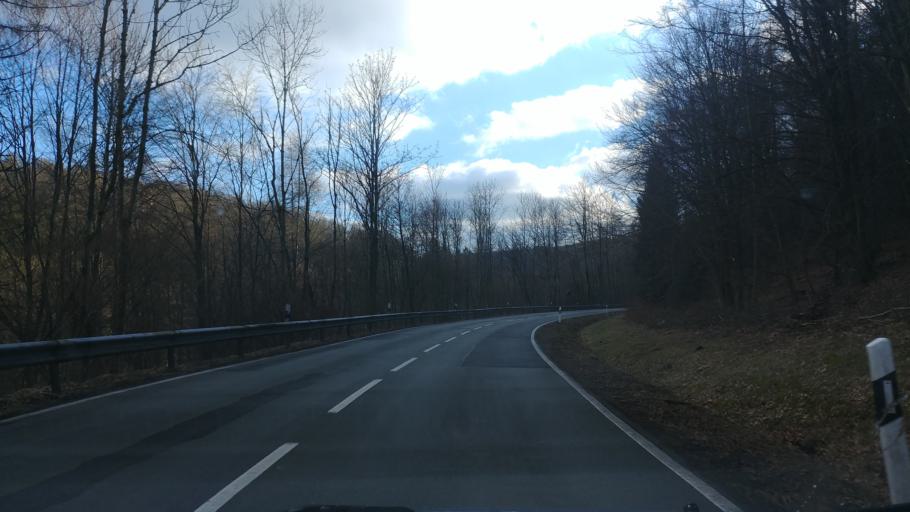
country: DE
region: Lower Saxony
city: Holzminden
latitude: 51.7870
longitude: 9.4785
